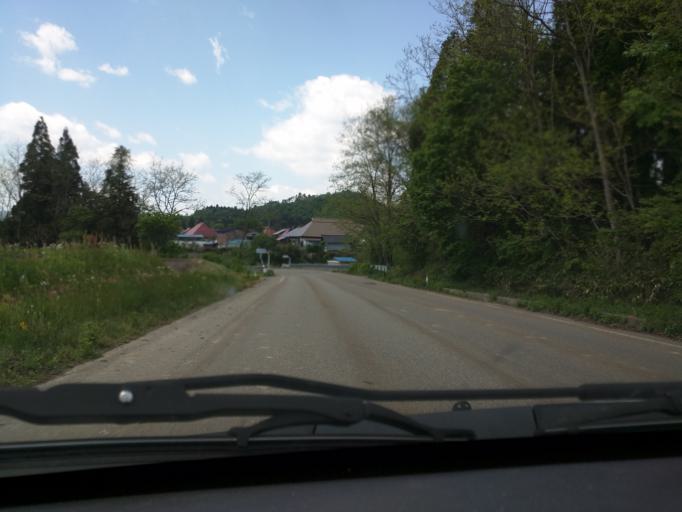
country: JP
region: Fukushima
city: Kitakata
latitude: 37.6408
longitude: 139.7921
